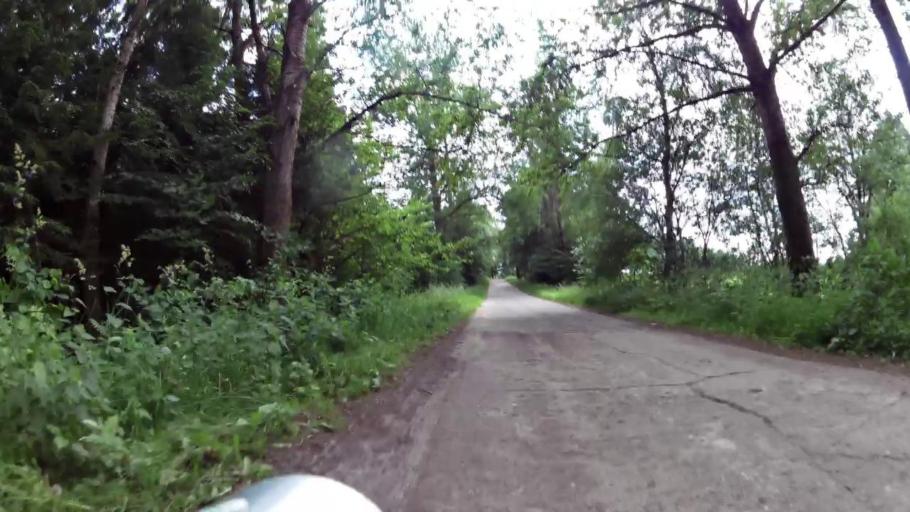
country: PL
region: West Pomeranian Voivodeship
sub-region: Powiat koszalinski
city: Bobolice
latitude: 53.9651
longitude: 16.7043
